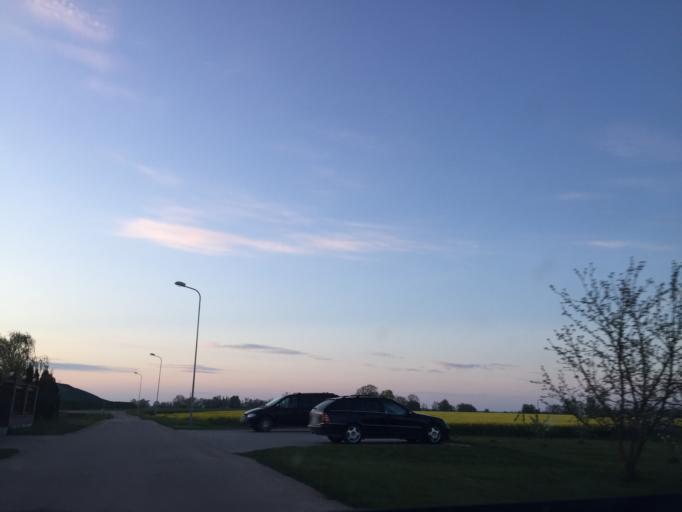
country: LV
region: Rundales
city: Pilsrundale
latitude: 56.4441
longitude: 24.0578
